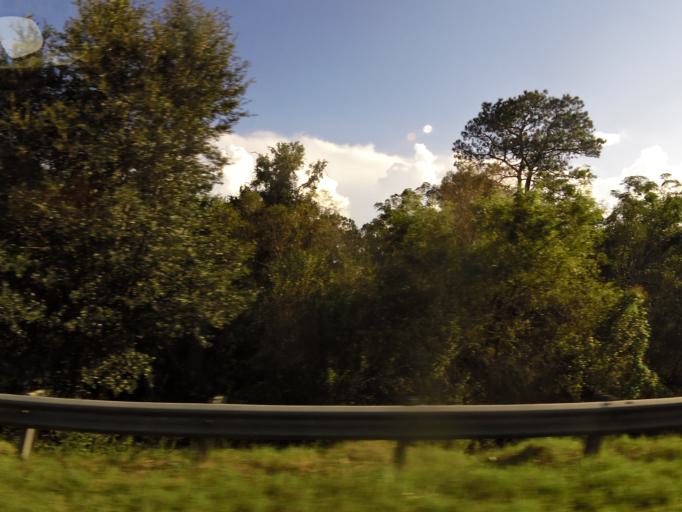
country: US
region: Georgia
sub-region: Brooks County
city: Quitman
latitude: 30.7865
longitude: -83.5160
